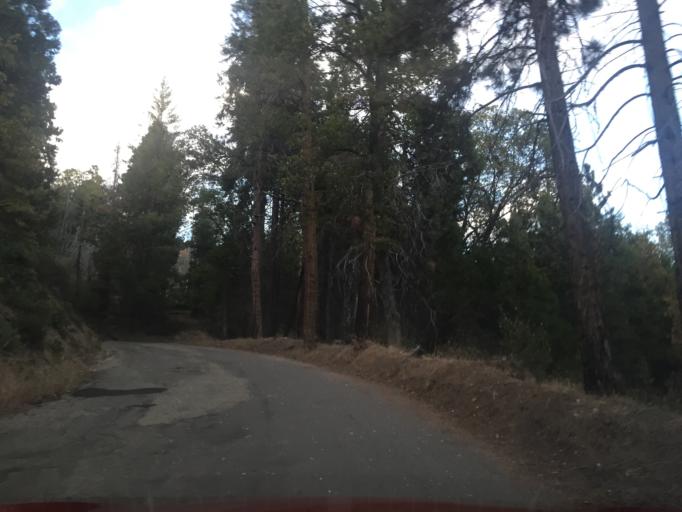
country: US
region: California
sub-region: Tulare County
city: Three Rivers
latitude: 36.4515
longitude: -118.6897
